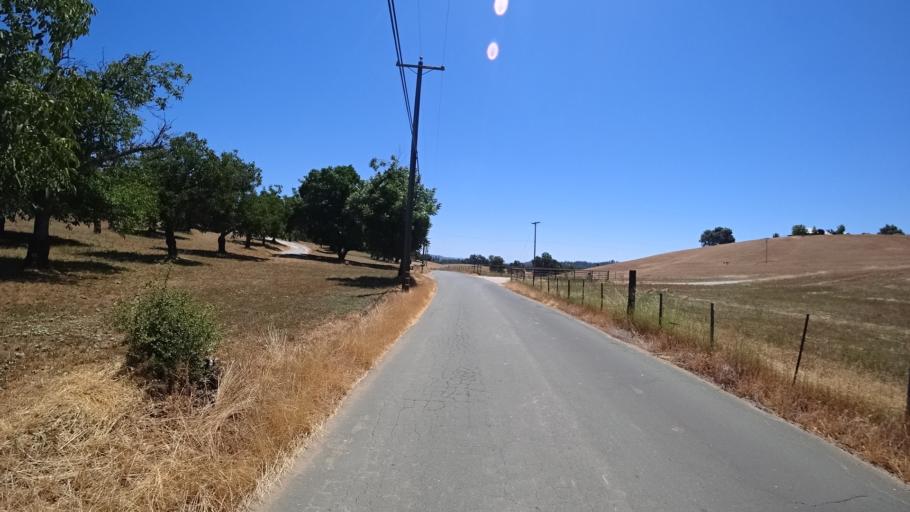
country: US
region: California
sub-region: Calaveras County
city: Mountain Ranch
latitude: 38.2334
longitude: -120.5522
